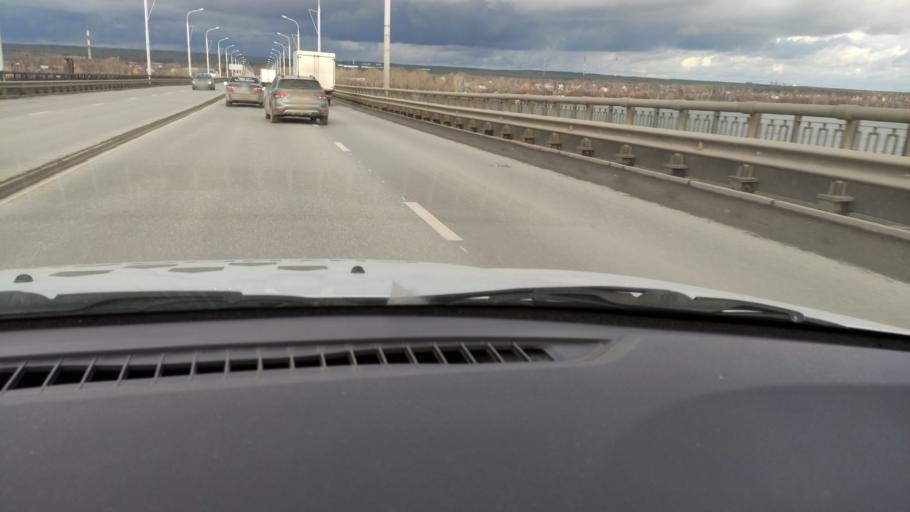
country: RU
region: Perm
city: Perm
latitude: 58.0176
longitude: 56.2227
